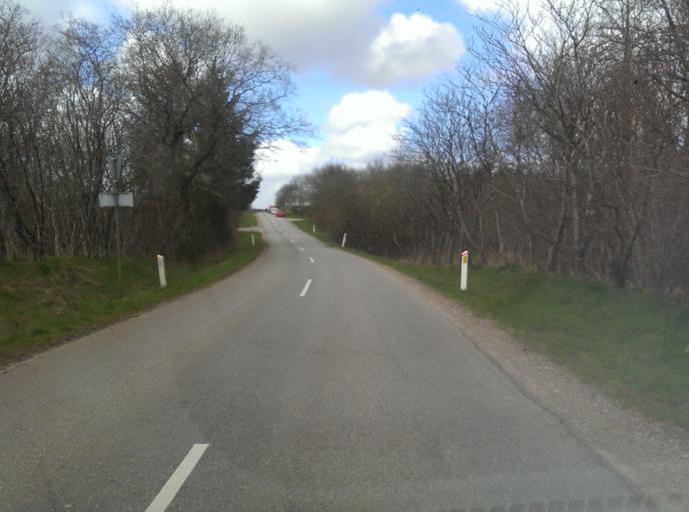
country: DK
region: South Denmark
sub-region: Varde Kommune
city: Varde
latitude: 55.5613
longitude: 8.4768
